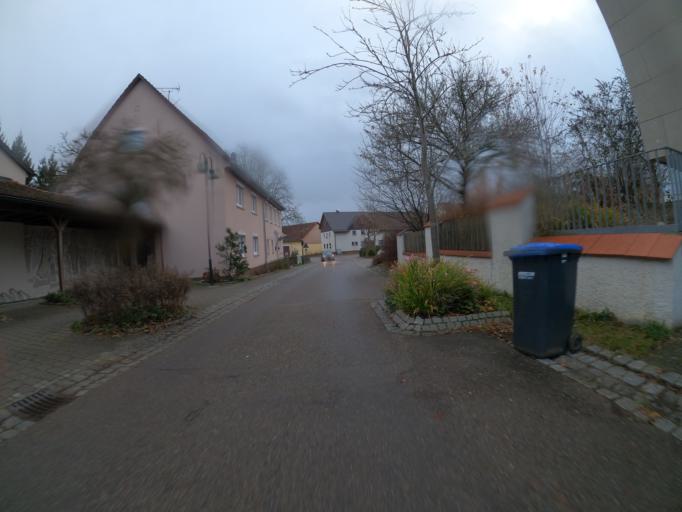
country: DE
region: Baden-Wuerttemberg
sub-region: Regierungsbezirk Stuttgart
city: Waschenbeuren
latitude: 48.7611
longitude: 9.6846
